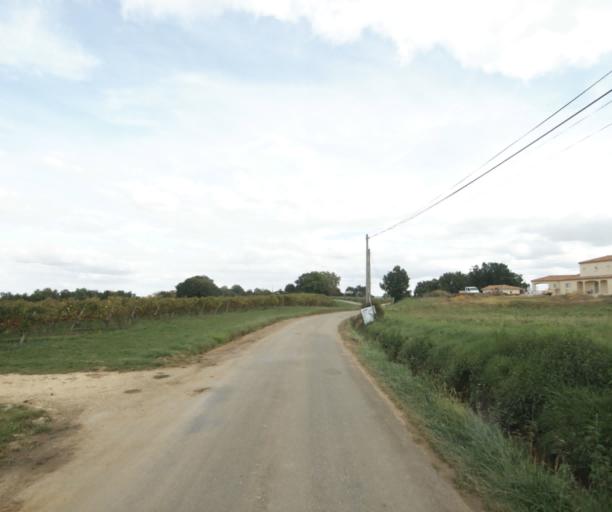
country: FR
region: Midi-Pyrenees
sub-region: Departement du Gers
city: Gondrin
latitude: 43.8741
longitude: 0.2424
